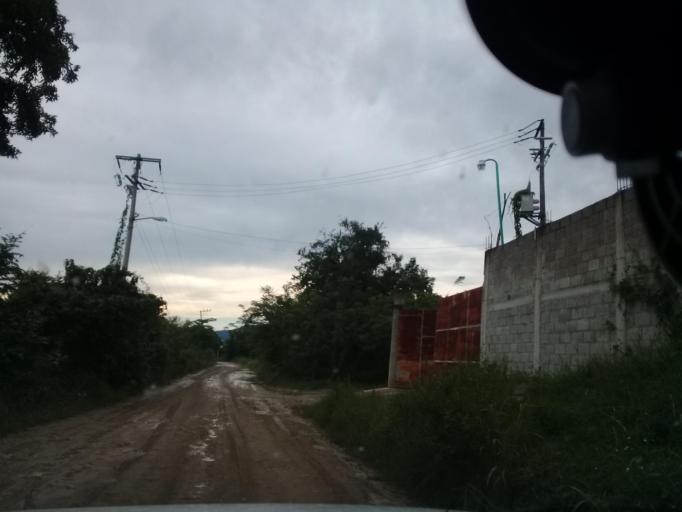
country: MX
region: Hidalgo
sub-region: Huejutla de Reyes
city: Parque de Poblamiento Solidaridad
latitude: 21.1561
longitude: -98.3759
